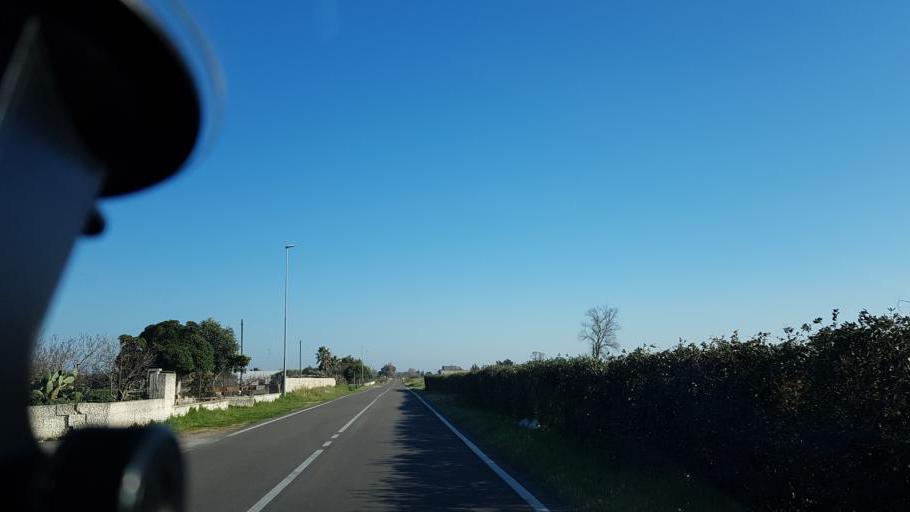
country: IT
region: Apulia
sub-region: Provincia di Lecce
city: Merine
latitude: 40.4177
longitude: 18.2508
